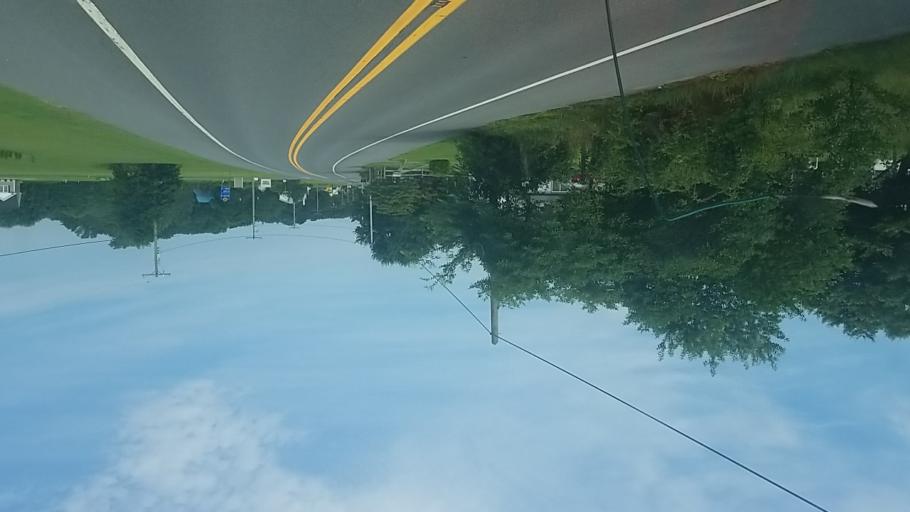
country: US
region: Delaware
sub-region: Sussex County
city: Ocean View
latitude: 38.5478
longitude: -75.1565
